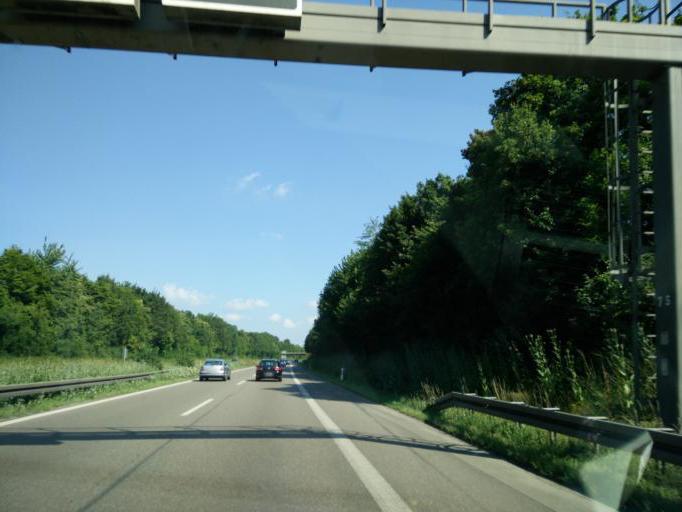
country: DE
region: Baden-Wuerttemberg
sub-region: Regierungsbezirk Stuttgart
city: Leinfelden-Echterdingen
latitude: 48.6778
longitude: 9.1837
